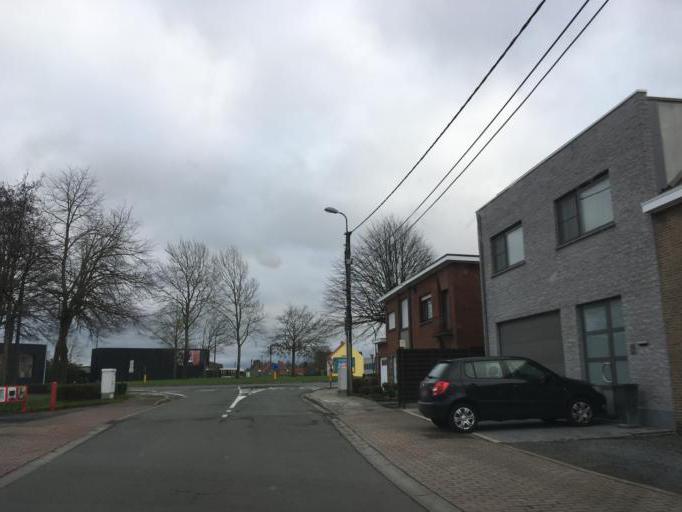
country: BE
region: Flanders
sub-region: Provincie West-Vlaanderen
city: Roeselare
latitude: 50.9732
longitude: 3.1183
